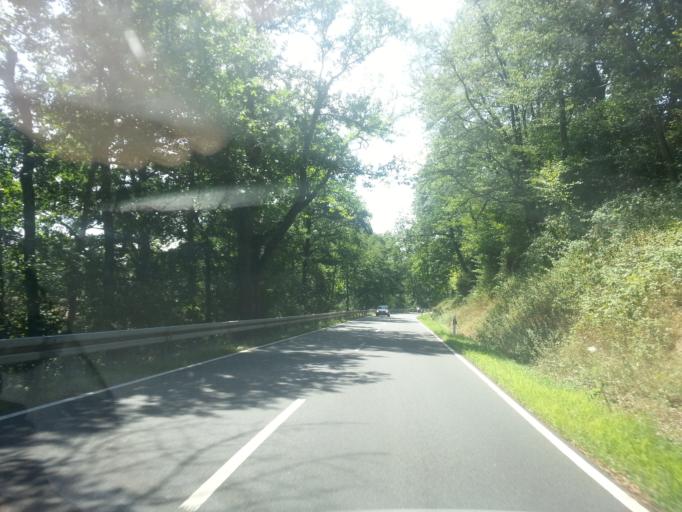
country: DE
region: Hesse
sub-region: Regierungsbezirk Darmstadt
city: Frankisch-Crumbach
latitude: 49.7218
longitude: 8.8745
